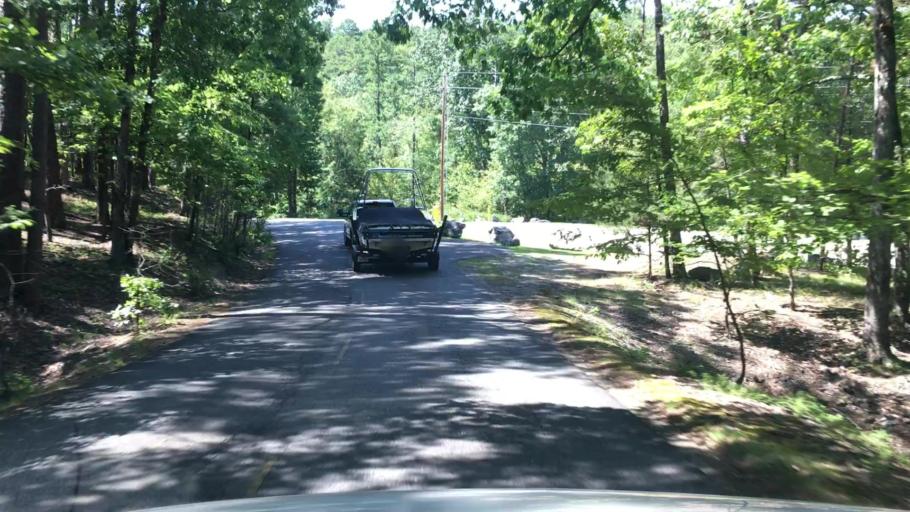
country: US
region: Arkansas
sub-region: Garland County
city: Piney
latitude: 34.5427
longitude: -93.3575
